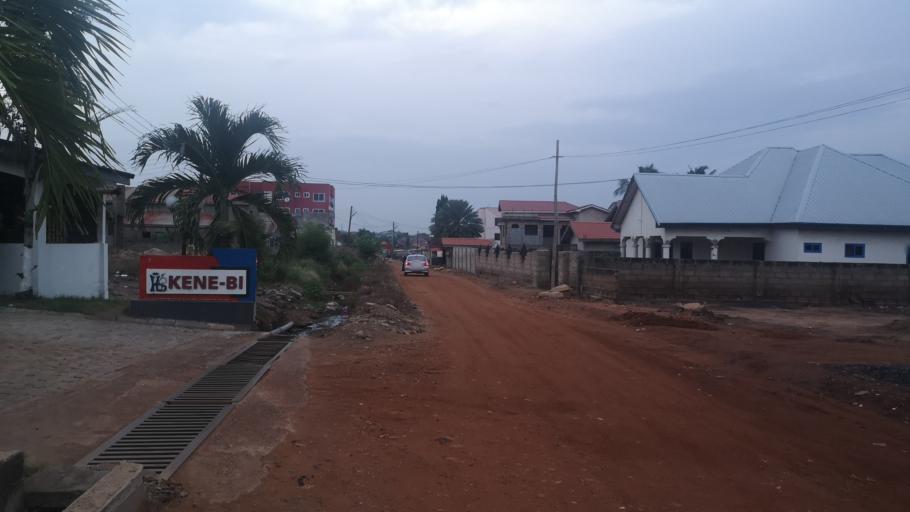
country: GH
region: Greater Accra
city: Nungua
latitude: 5.6378
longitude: -0.0786
